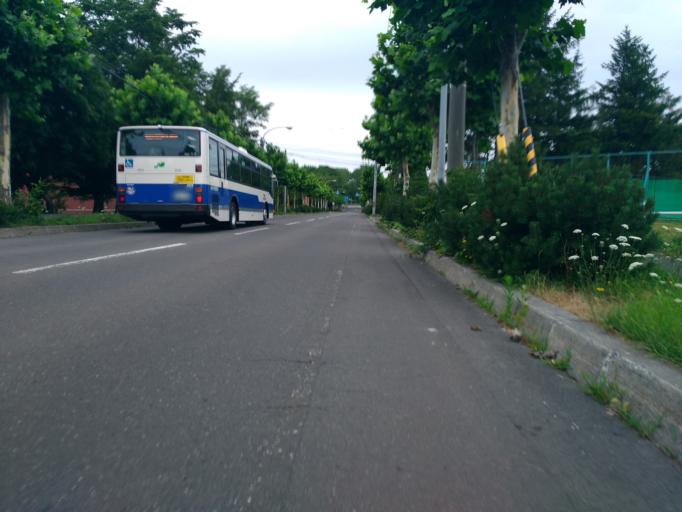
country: JP
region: Hokkaido
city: Ebetsu
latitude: 43.0690
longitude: 141.5020
